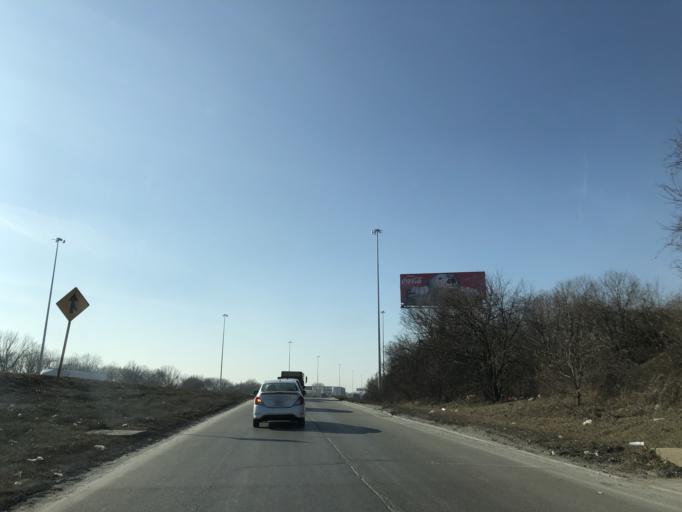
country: US
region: Illinois
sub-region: Cook County
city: Cicero
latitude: 41.8169
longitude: -87.7454
